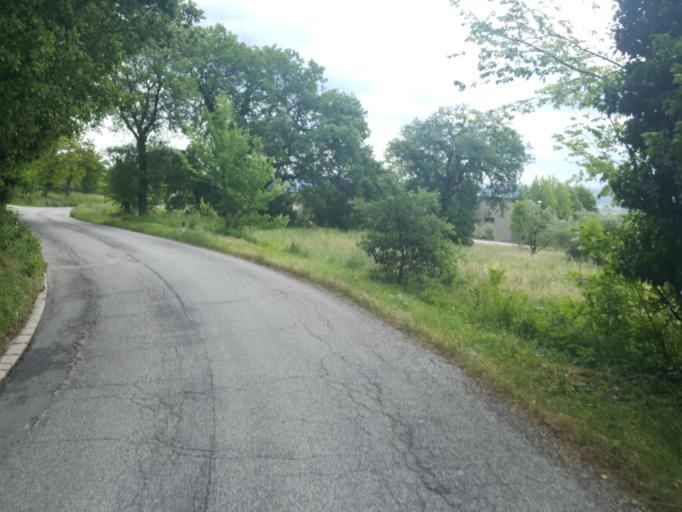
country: IT
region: The Marches
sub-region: Provincia di Macerata
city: Pollenza
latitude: 43.2586
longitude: 13.3607
